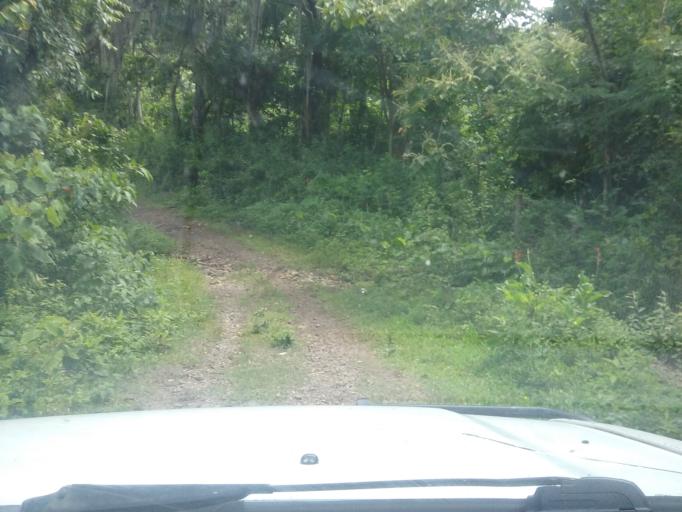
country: NI
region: Matagalpa
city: Matagalpa
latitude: 12.8680
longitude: -85.9162
